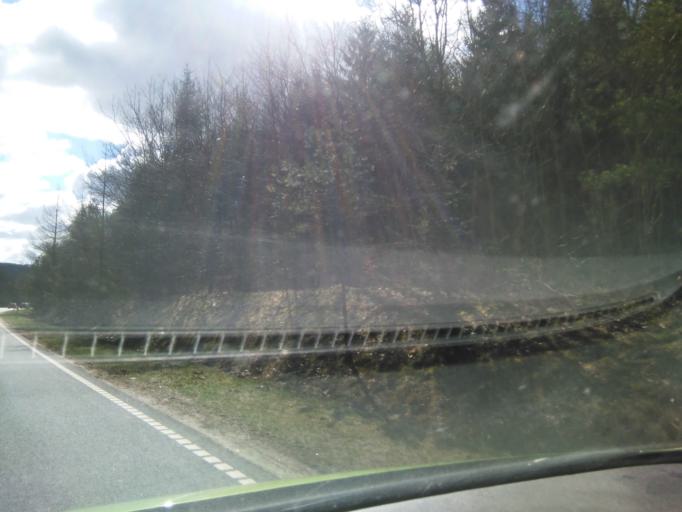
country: DK
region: Central Jutland
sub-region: Silkeborg Kommune
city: Virklund
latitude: 56.0706
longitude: 9.5783
